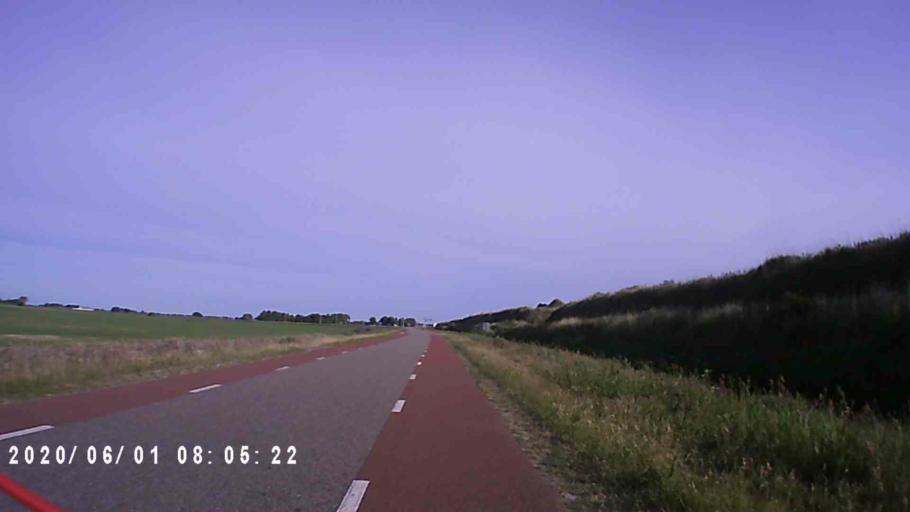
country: NL
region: Friesland
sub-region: Gemeente Tytsjerksteradiel
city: Oentsjerk
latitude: 53.2793
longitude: 5.9101
